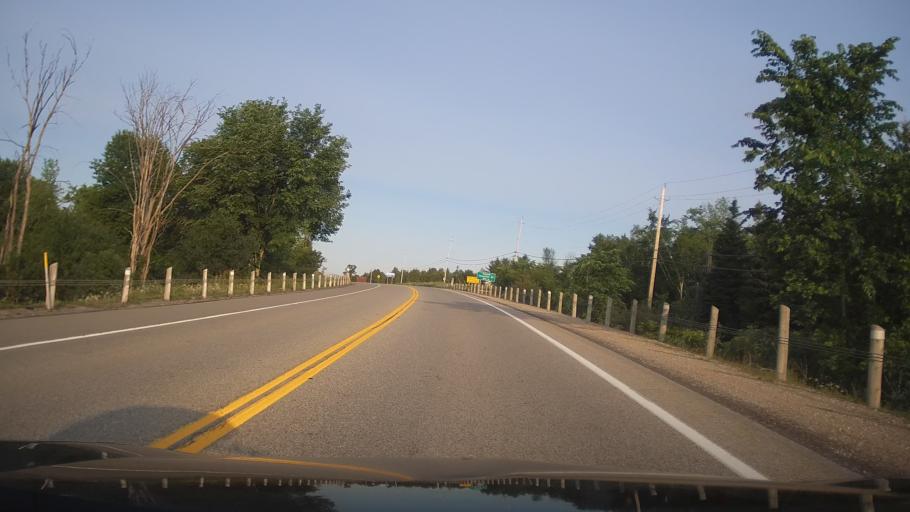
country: CA
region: Ontario
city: Carleton Place
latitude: 45.1330
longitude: -76.1798
